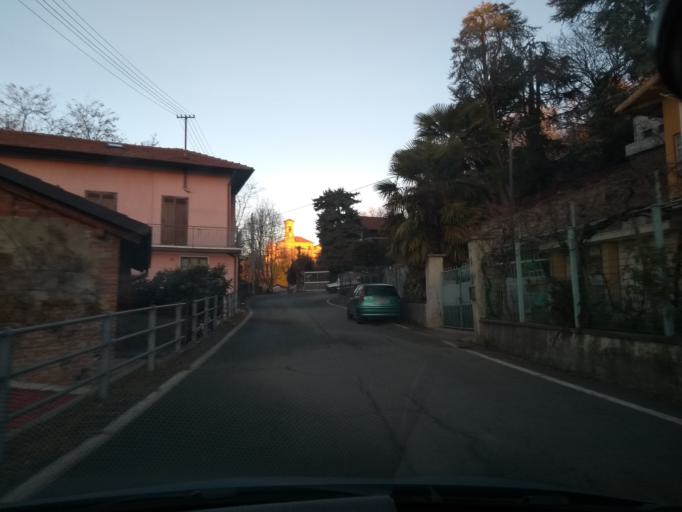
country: IT
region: Piedmont
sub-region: Provincia di Torino
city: Balangero
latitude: 45.2745
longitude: 7.5243
